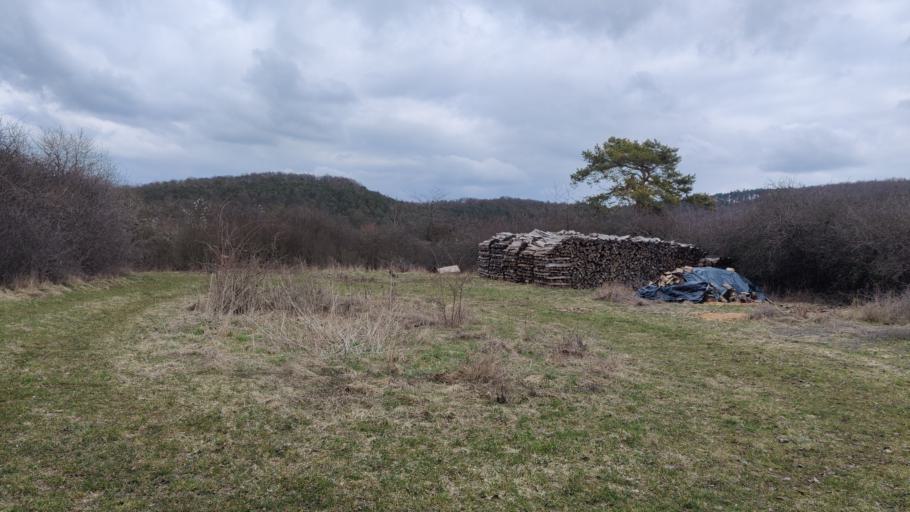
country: DE
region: Bavaria
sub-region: Regierungsbezirk Unterfranken
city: Bad Kissingen
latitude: 50.2099
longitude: 10.0994
